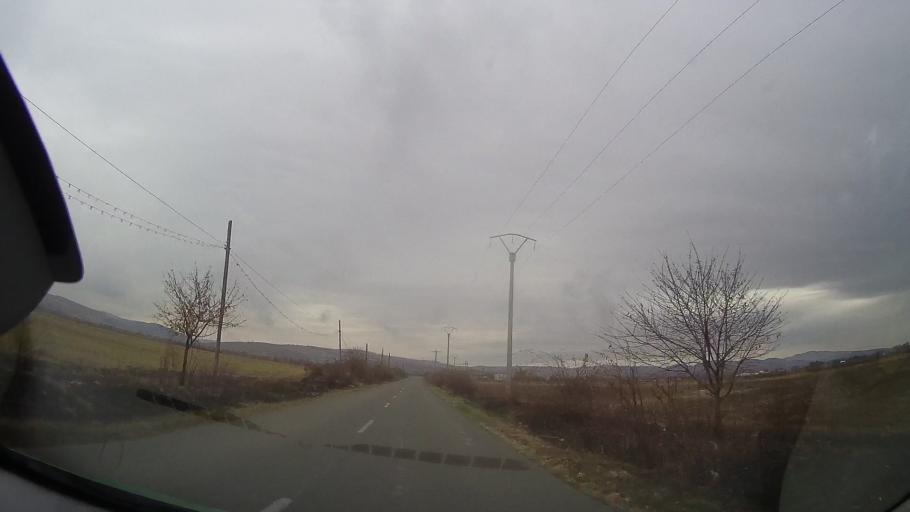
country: RO
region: Prahova
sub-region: Comuna Fantanele
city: Fantanele
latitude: 45.0193
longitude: 26.3804
